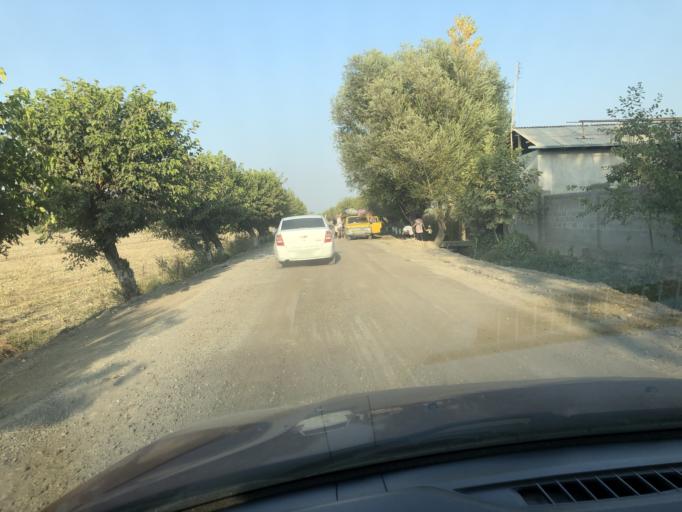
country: UZ
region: Namangan
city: Uychi
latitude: 41.0641
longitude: 71.9882
